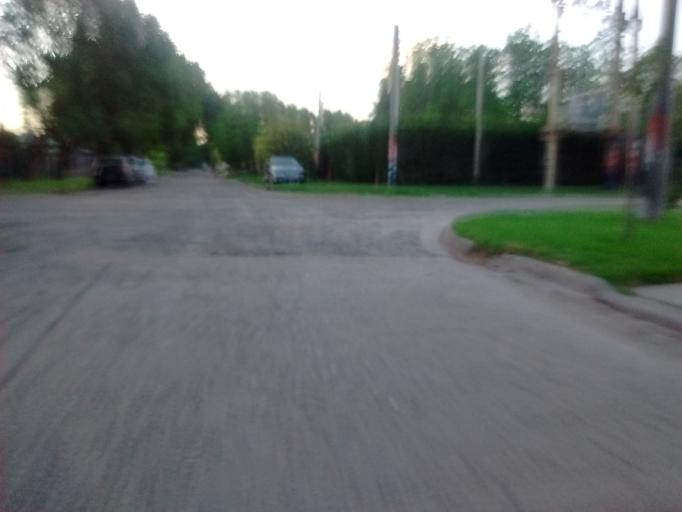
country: AR
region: Santa Fe
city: Funes
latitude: -32.9136
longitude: -60.8165
